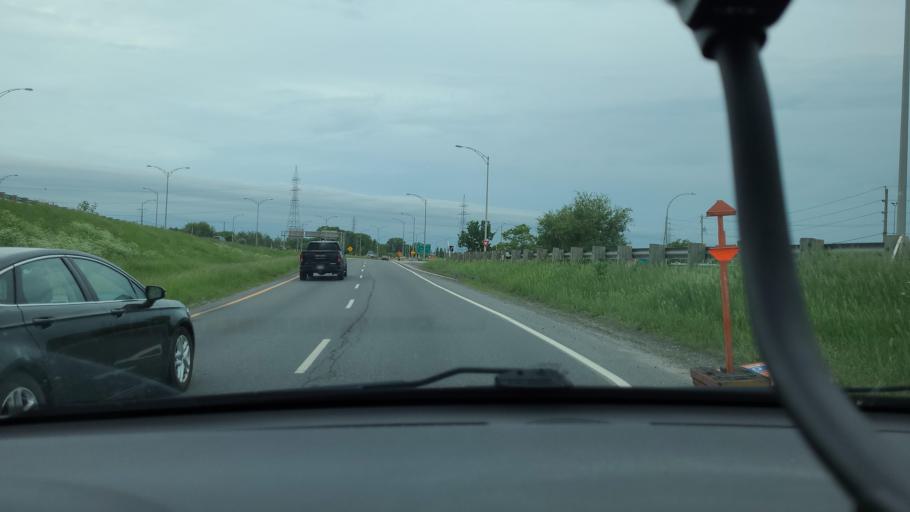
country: CA
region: Quebec
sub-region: Monteregie
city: Candiac
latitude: 45.3966
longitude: -73.5093
